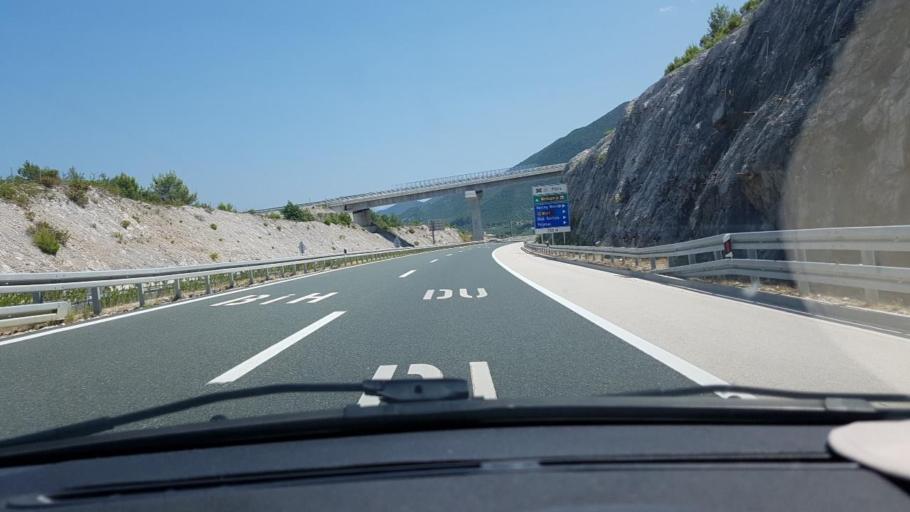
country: BA
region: Federation of Bosnia and Herzegovina
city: Ljubuski
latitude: 43.1588
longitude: 17.4770
